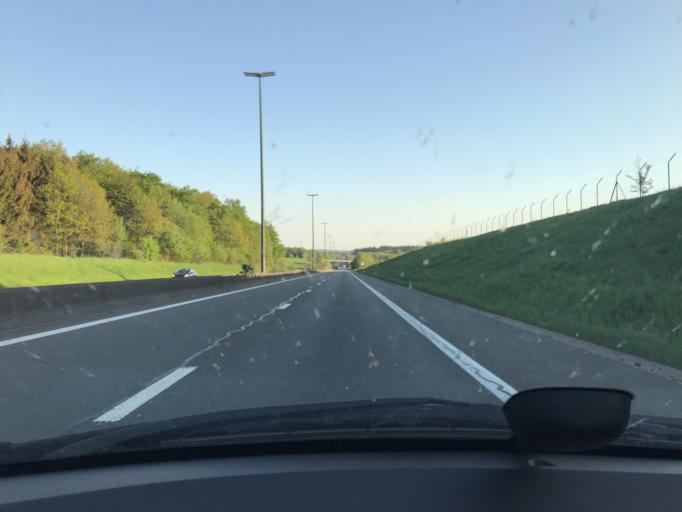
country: BE
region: Wallonia
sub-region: Province du Luxembourg
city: Libin
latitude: 49.9672
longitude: 5.2385
